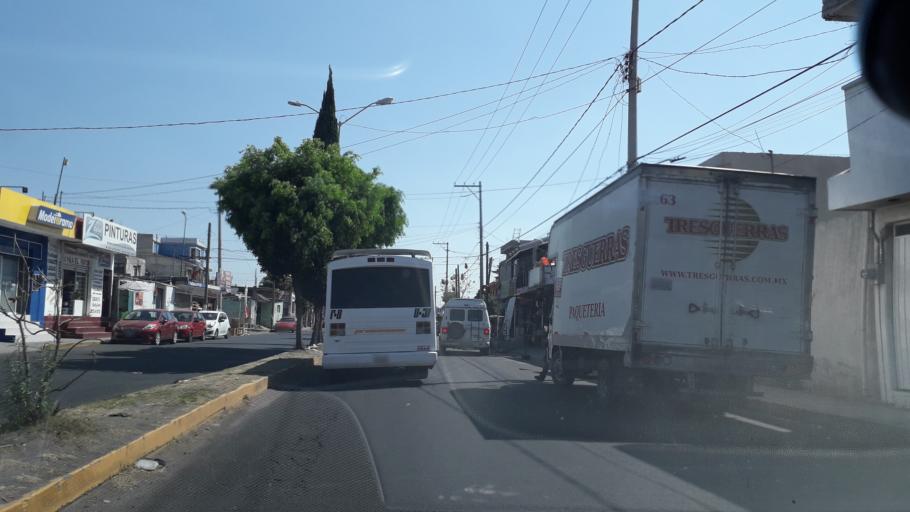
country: MX
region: Puebla
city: Puebla
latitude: 18.9906
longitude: -98.2143
